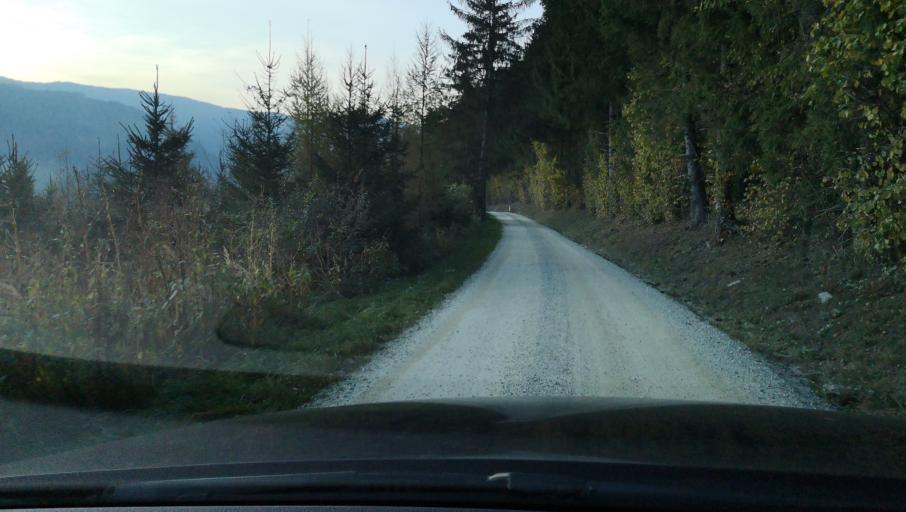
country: AT
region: Styria
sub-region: Politischer Bezirk Weiz
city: Birkfeld
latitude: 47.3551
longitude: 15.6800
